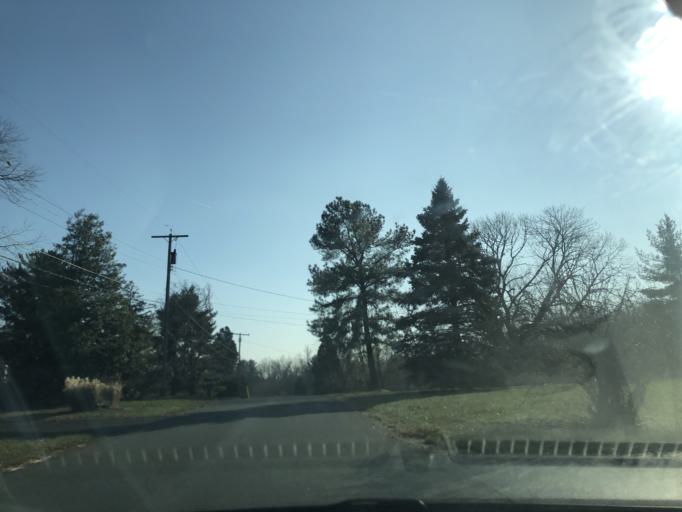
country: US
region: Maryland
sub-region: Montgomery County
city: Burtonsville
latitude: 39.1063
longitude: -76.9365
